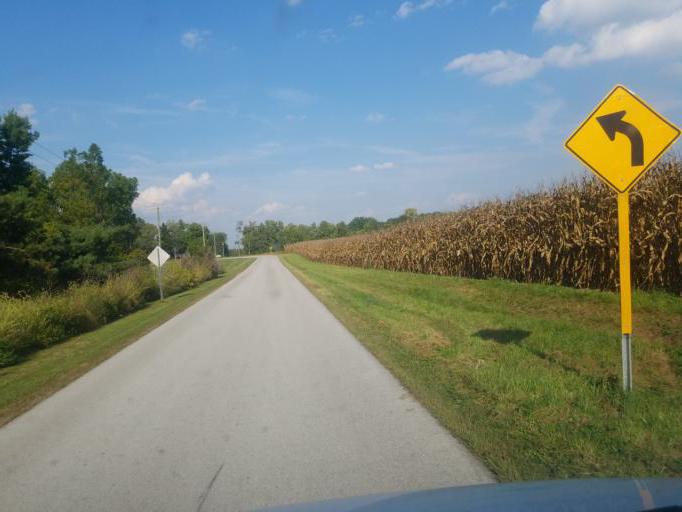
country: US
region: Ohio
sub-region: Hancock County
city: Arlington
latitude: 40.8809
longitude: -83.5698
